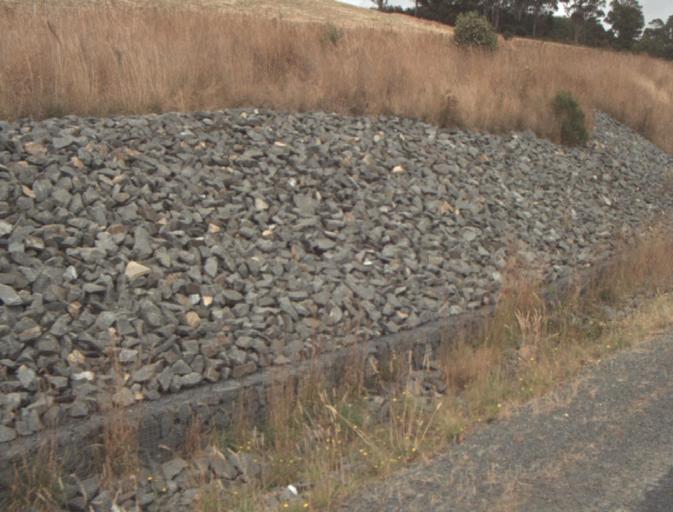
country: AU
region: Tasmania
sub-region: Dorset
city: Bridport
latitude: -41.1661
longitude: 147.2357
